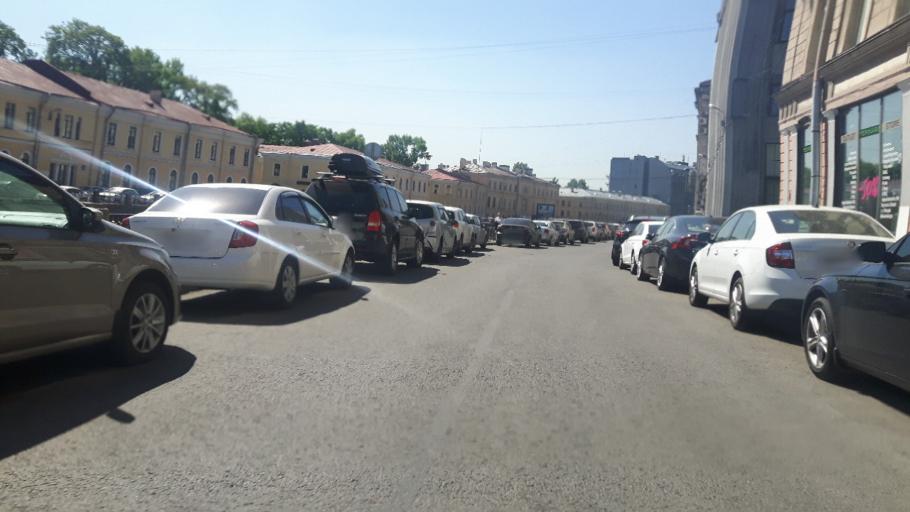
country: RU
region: St.-Petersburg
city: Saint Petersburg
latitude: 59.9347
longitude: 30.3180
